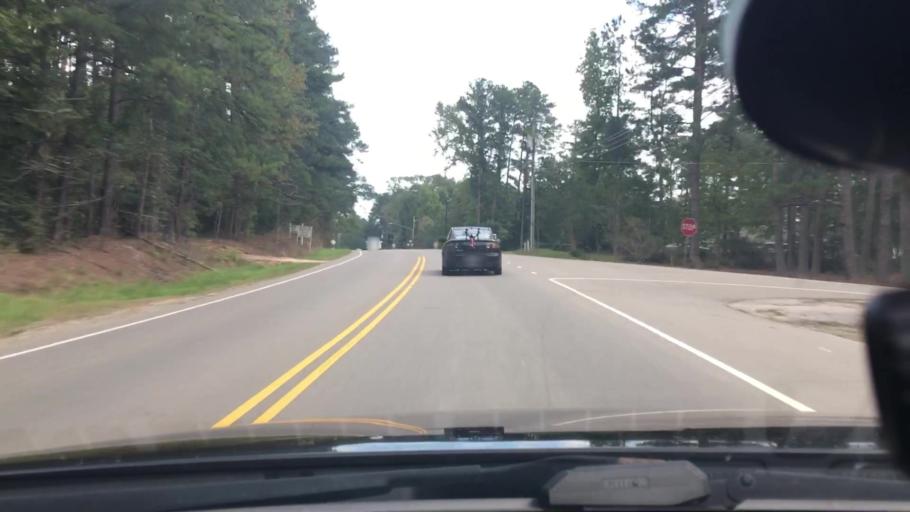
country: US
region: North Carolina
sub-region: Moore County
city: Carthage
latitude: 35.3574
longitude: -79.4324
